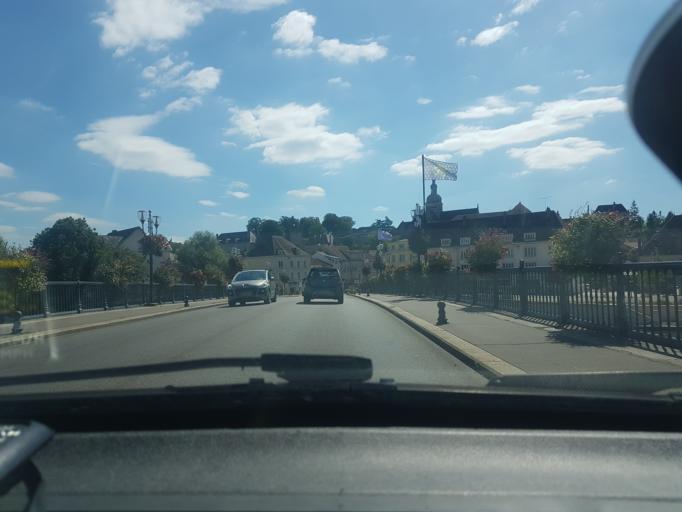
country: FR
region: Franche-Comte
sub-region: Departement de la Haute-Saone
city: Gray
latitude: 47.4496
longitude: 5.5912
